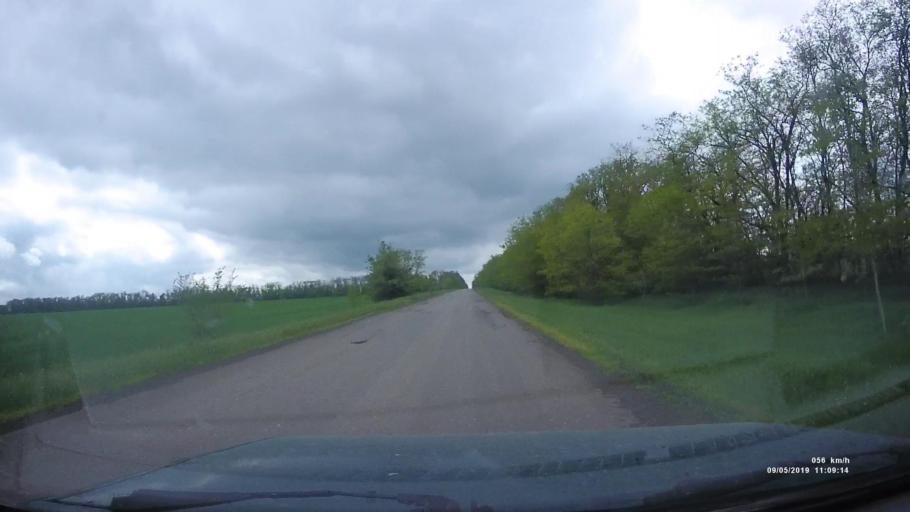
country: RU
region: Krasnodarskiy
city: Kanelovskaya
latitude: 46.7849
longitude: 39.2117
